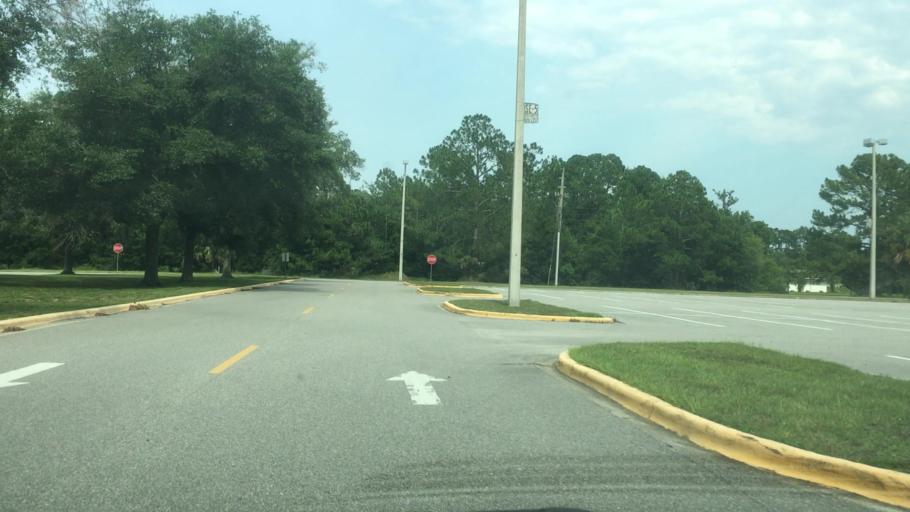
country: US
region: Florida
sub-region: Duval County
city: Neptune Beach
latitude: 30.2922
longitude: -81.5064
